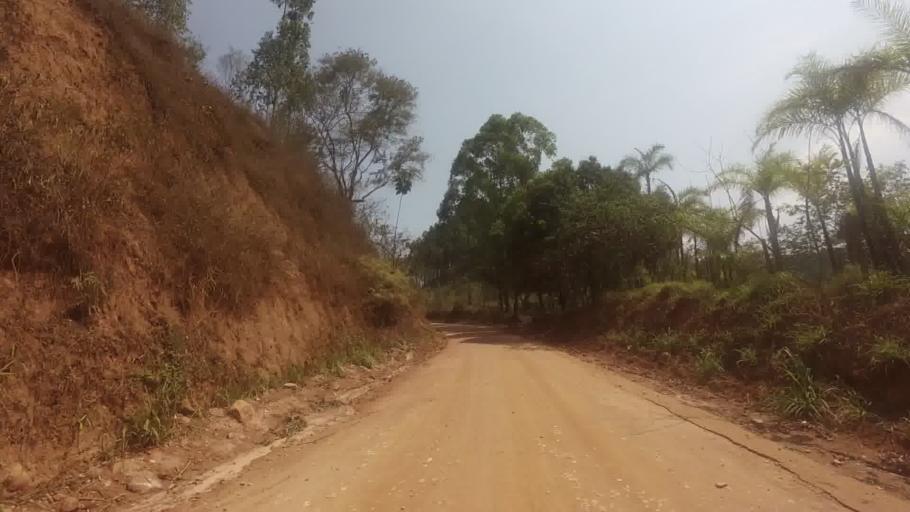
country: BR
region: Espirito Santo
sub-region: Mimoso Do Sul
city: Mimoso do Sul
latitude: -20.9450
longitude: -41.4050
